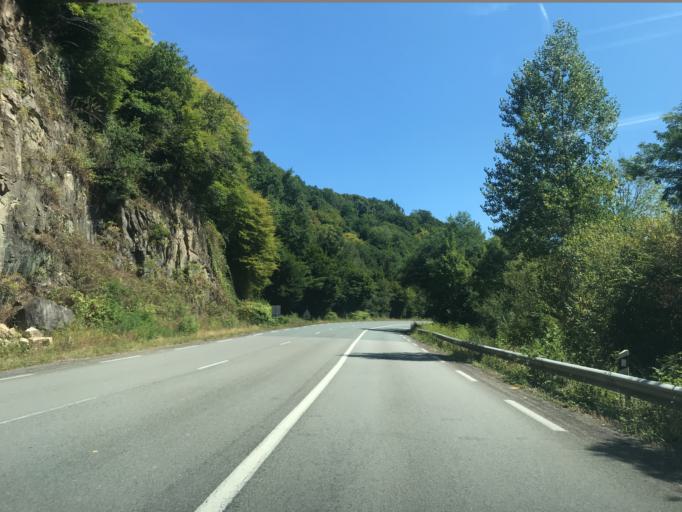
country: FR
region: Limousin
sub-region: Departement de la Correze
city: Chameyrat
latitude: 45.2326
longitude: 1.7205
